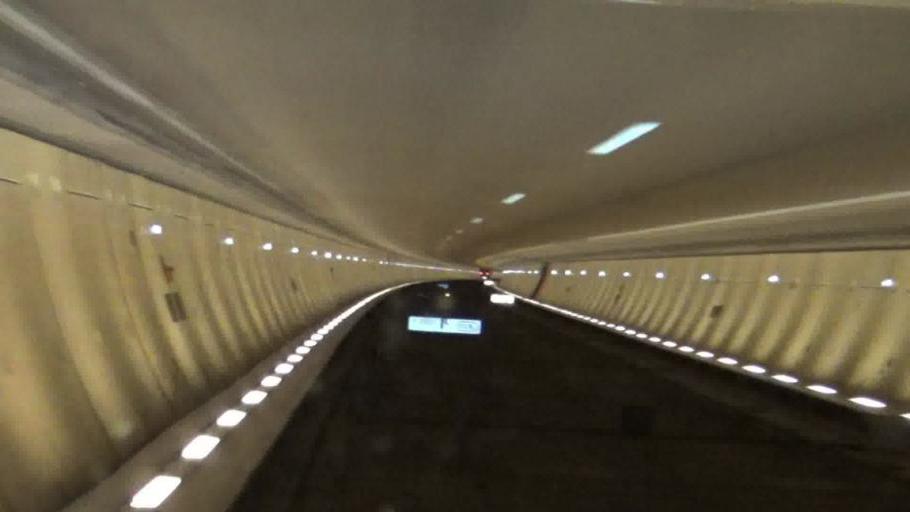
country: FR
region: Ile-de-France
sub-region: Departement des Hauts-de-Seine
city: Marnes-la-Coquette
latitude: 48.8198
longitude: 2.1548
